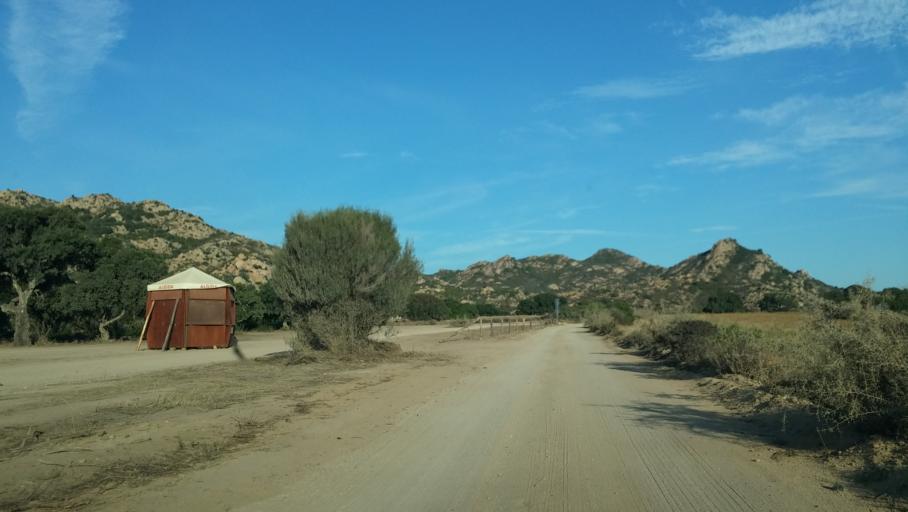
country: IT
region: Sardinia
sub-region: Provincia di Nuoro
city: La Caletta
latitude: 40.4811
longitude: 9.8063
